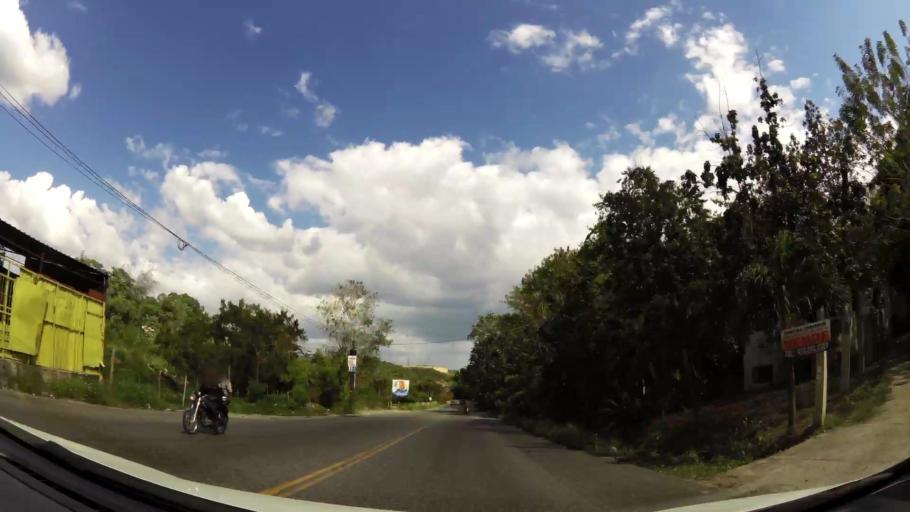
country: DO
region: San Cristobal
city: Bajos de Haina
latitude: 18.4274
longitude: -70.0591
